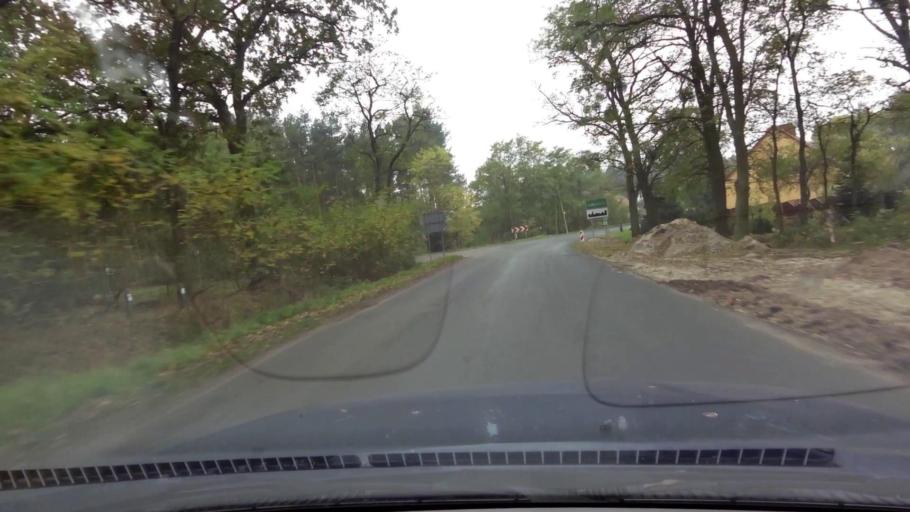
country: PL
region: West Pomeranian Voivodeship
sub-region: Powiat goleniowski
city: Goleniow
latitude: 53.5110
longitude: 14.7412
